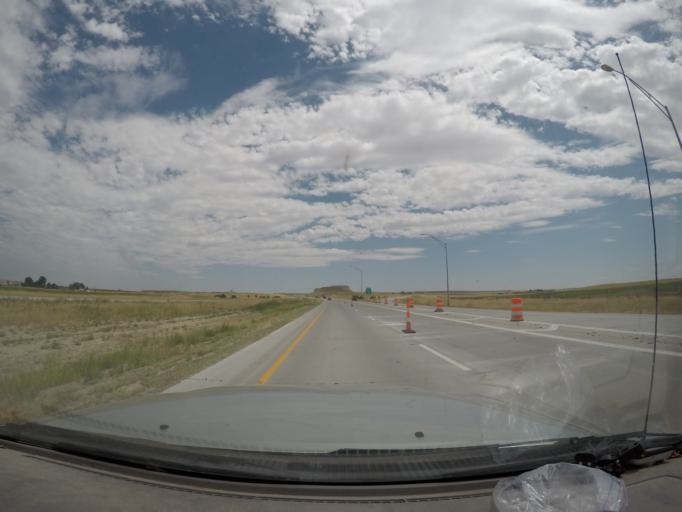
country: US
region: Nebraska
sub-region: Cheyenne County
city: Sidney
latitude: 41.1280
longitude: -103.0370
